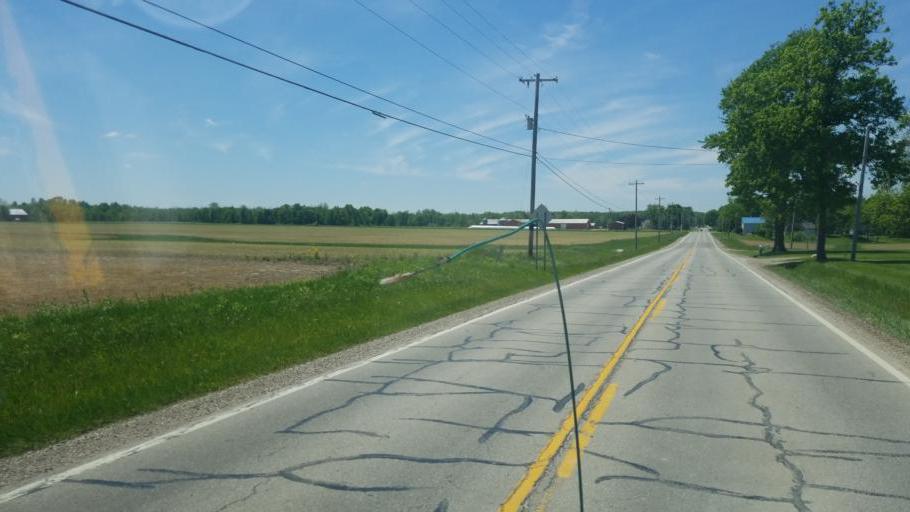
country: US
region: Ohio
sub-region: Huron County
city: Greenwich
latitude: 41.0301
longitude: -82.5313
